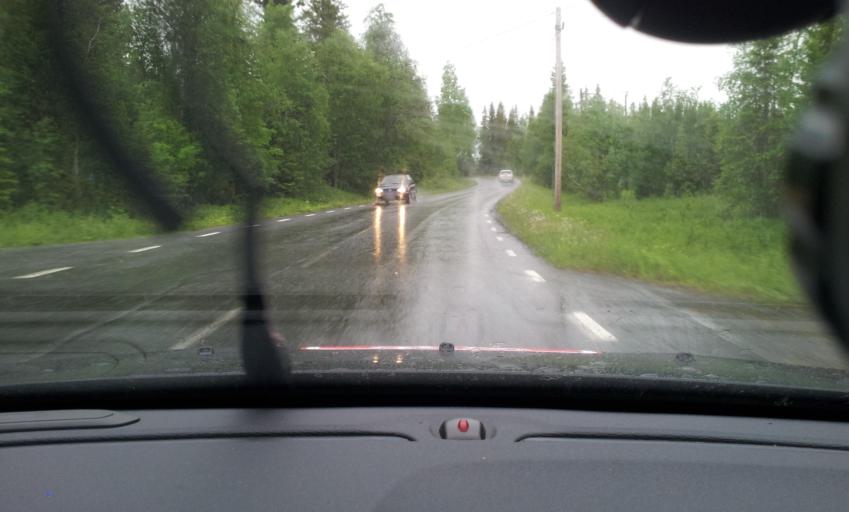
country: SE
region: Jaemtland
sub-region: Are Kommun
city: Are
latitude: 63.3141
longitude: 13.1644
